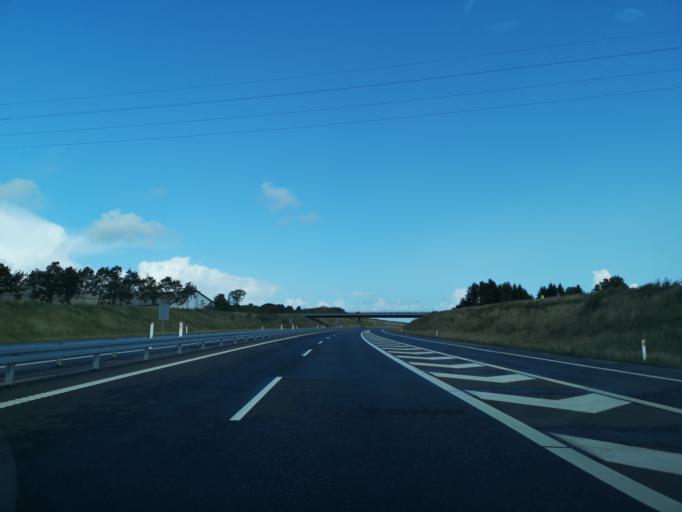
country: DK
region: Central Jutland
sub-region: Herning Kommune
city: Snejbjerg
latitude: 56.1322
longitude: 8.8719
